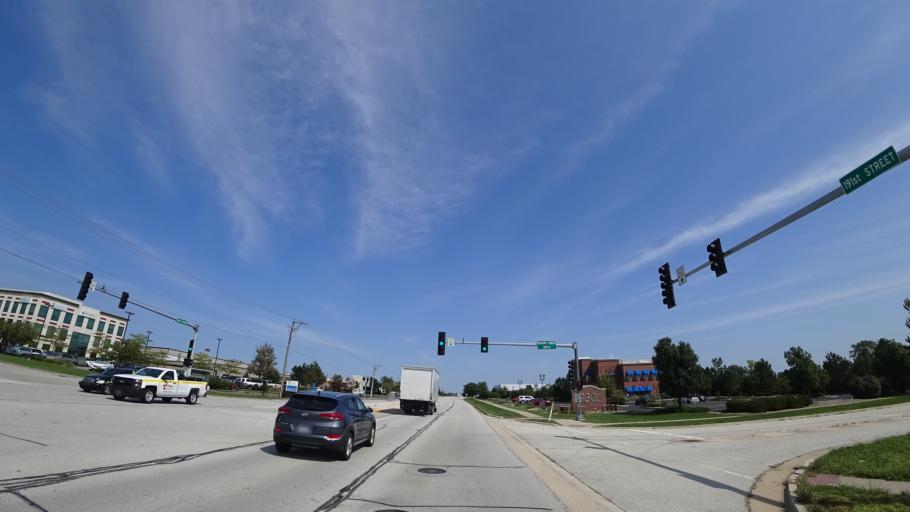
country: US
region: Illinois
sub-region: Cook County
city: Orland Hills
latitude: 41.5431
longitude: -87.8432
